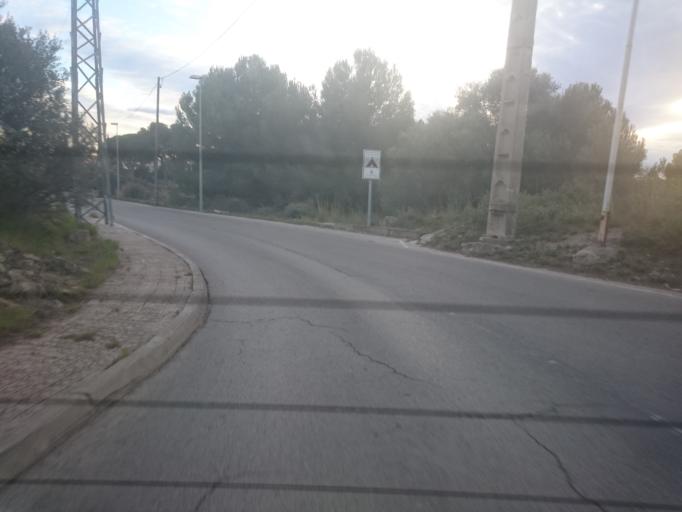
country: ES
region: Catalonia
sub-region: Provincia de Barcelona
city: Cubelles
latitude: 41.2090
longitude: 1.6867
